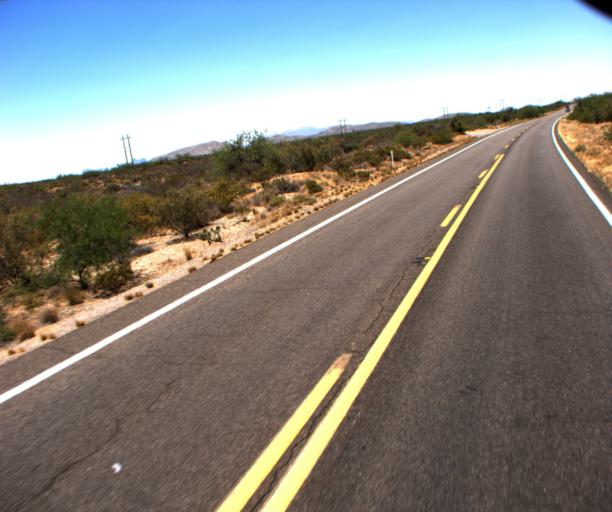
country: US
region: Arizona
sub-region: Pima County
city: Catalina
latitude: 32.6580
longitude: -111.0430
